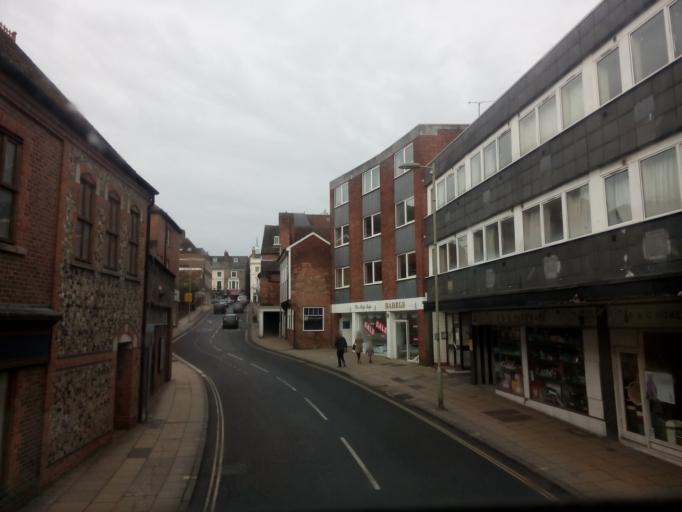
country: GB
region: England
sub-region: Hampshire
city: Winchester
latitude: 51.0630
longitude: -1.3144
